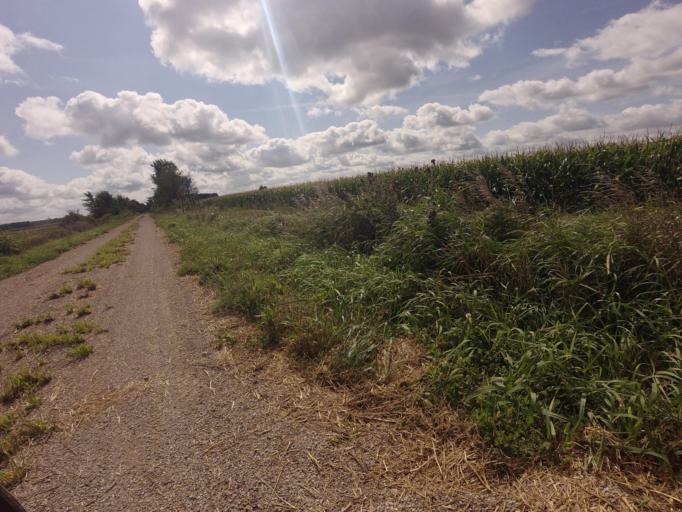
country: CA
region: Ontario
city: Huron East
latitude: 43.6517
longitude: -81.2304
